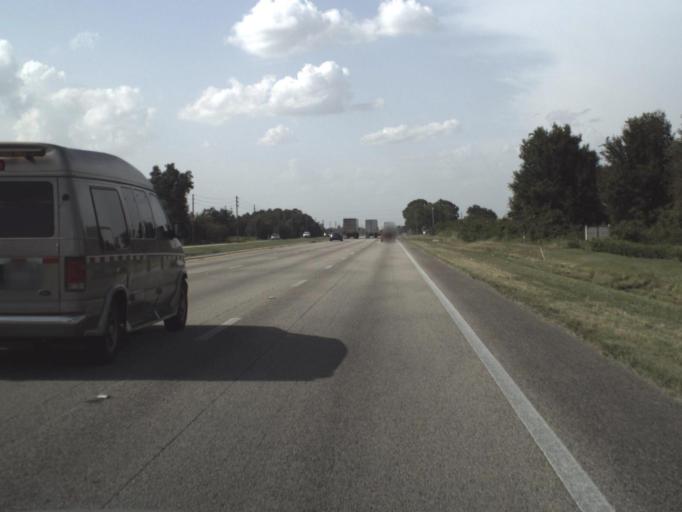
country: US
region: Florida
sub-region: Polk County
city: Lake Wales
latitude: 27.9359
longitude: -81.6105
